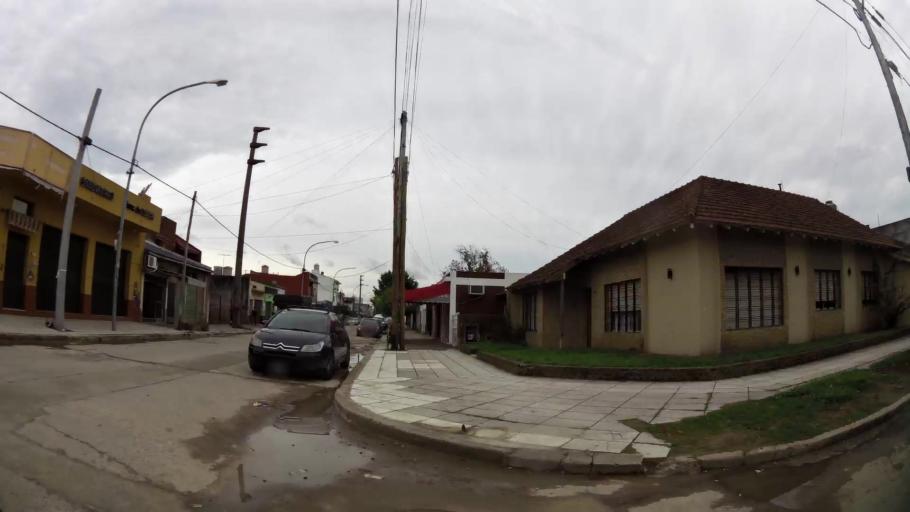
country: AR
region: Buenos Aires
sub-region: Partido de Lanus
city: Lanus
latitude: -34.7362
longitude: -58.3751
